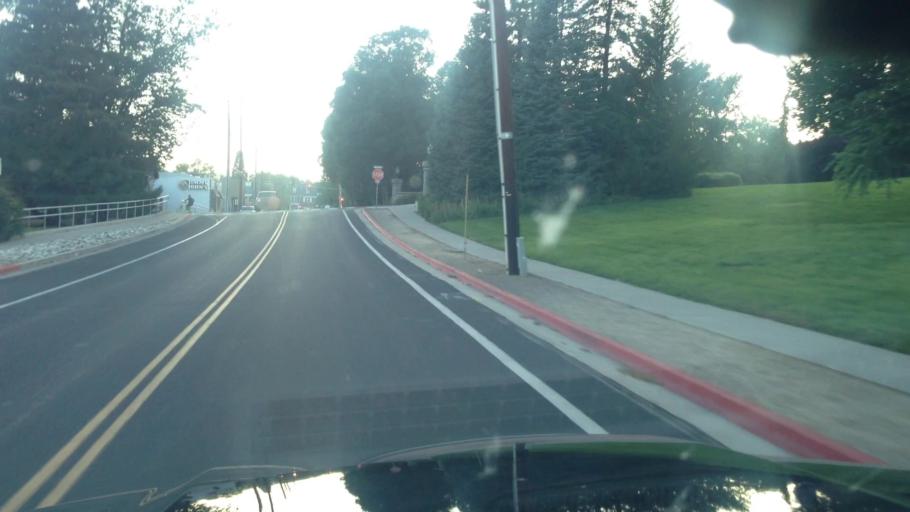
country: US
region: Nevada
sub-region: Washoe County
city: Reno
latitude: 39.5367
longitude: -119.8140
